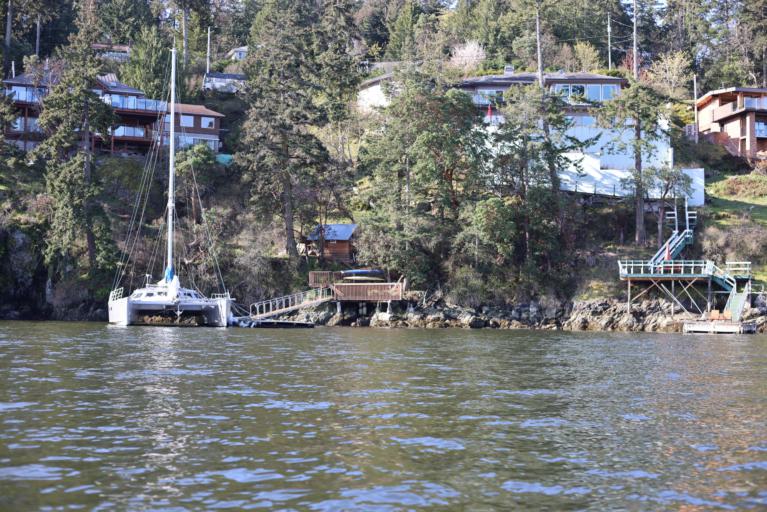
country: CA
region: British Columbia
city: North Saanich
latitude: 48.5767
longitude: -123.4827
